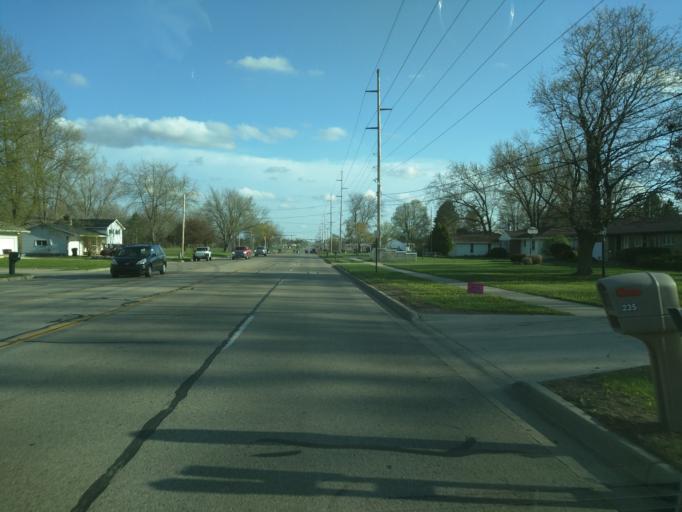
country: US
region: Michigan
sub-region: Eaton County
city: Waverly
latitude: 42.7357
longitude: -84.6423
